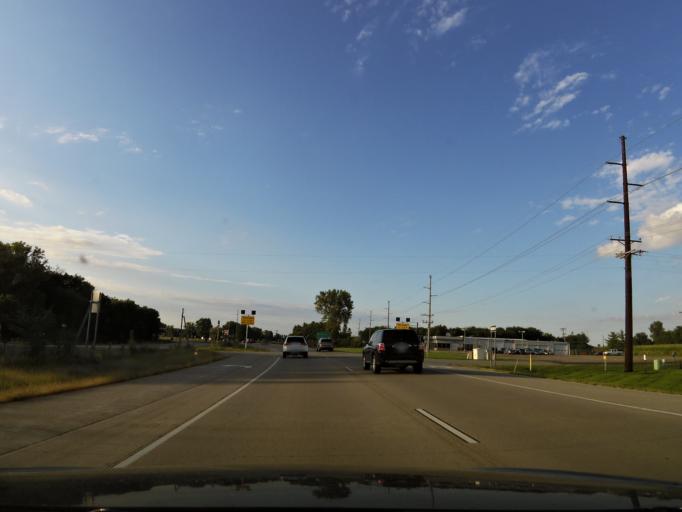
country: US
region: Minnesota
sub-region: Dakota County
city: Hastings
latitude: 44.7749
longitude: -92.8632
